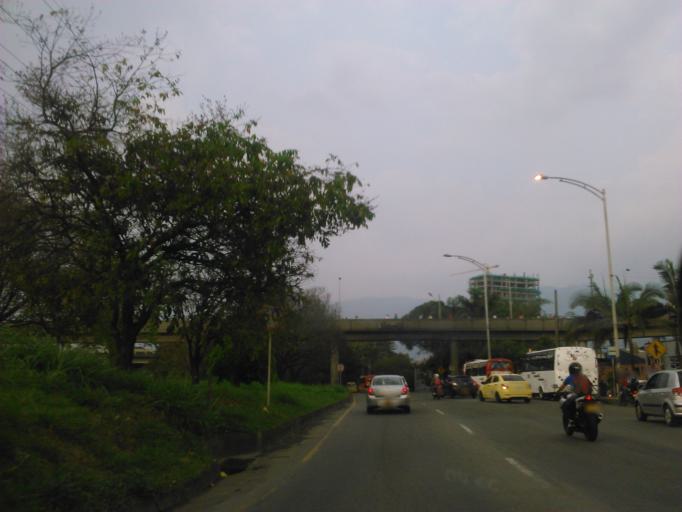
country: CO
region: Antioquia
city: Sabaneta
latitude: 6.1624
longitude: -75.6062
